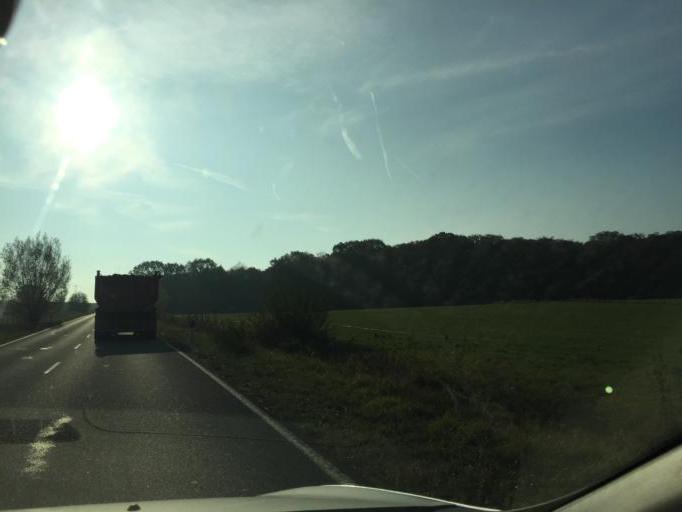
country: LU
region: Luxembourg
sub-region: Canton de Luxembourg
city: Contern
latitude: 49.5586
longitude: 6.2237
